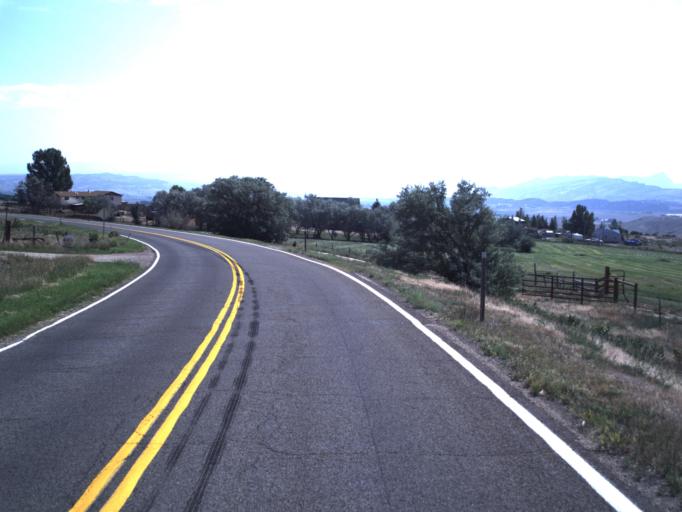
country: US
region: Utah
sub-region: Daggett County
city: Manila
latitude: 40.9773
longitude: -109.7505
